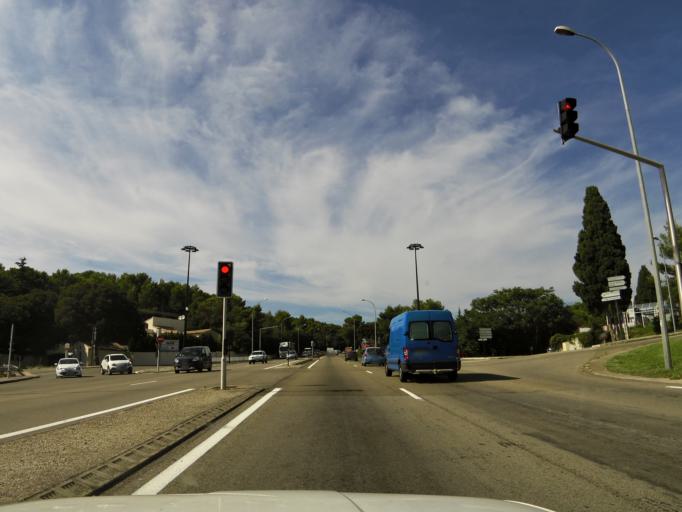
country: FR
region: Languedoc-Roussillon
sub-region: Departement du Gard
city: Nimes
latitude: 43.8304
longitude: 4.3233
